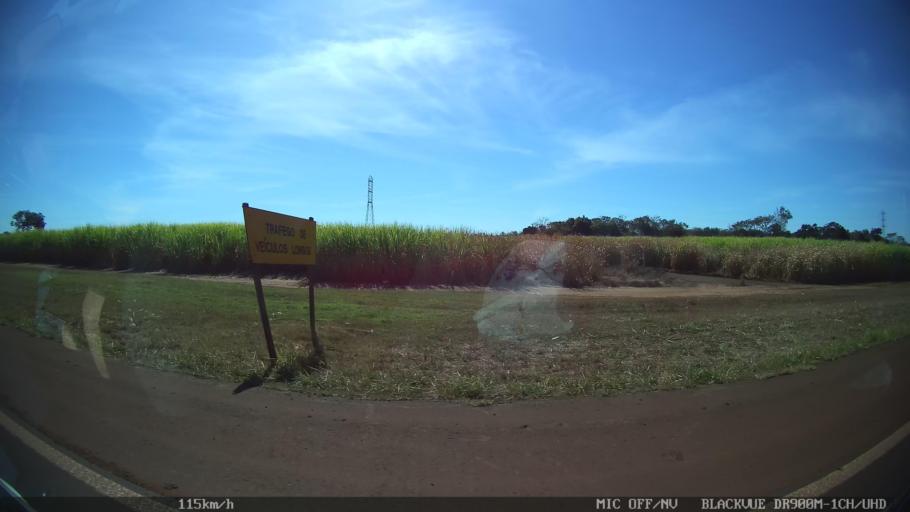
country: BR
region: Sao Paulo
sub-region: Guaira
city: Guaira
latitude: -20.4452
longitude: -48.2250
